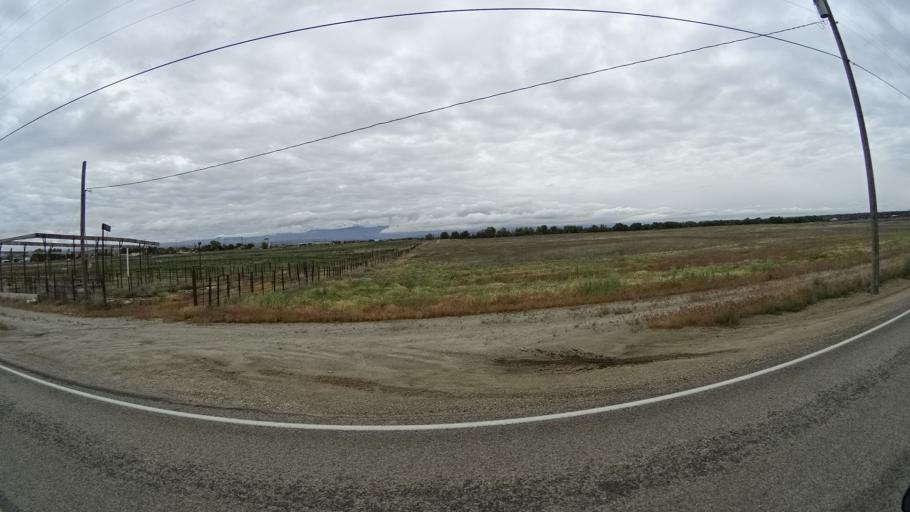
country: US
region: Idaho
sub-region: Ada County
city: Star
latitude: 43.7175
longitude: -116.4436
